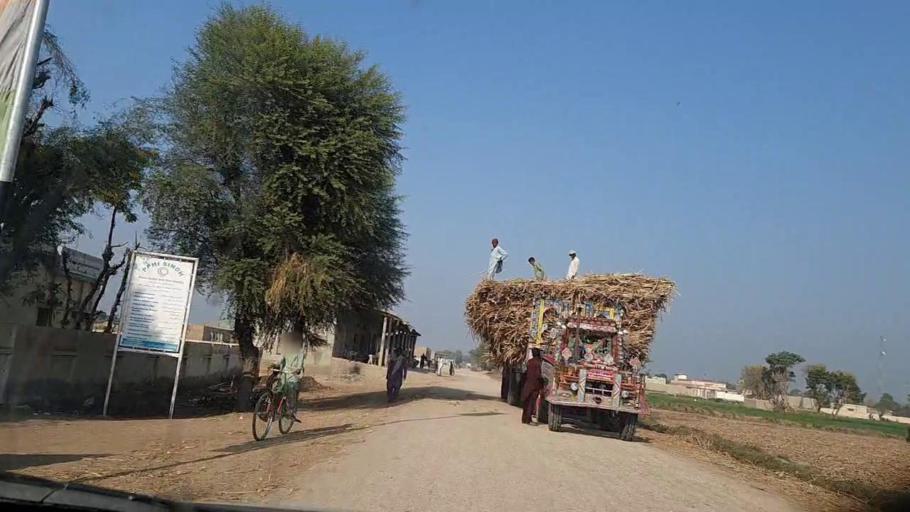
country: PK
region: Sindh
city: Moro
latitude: 26.7860
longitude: 67.9383
